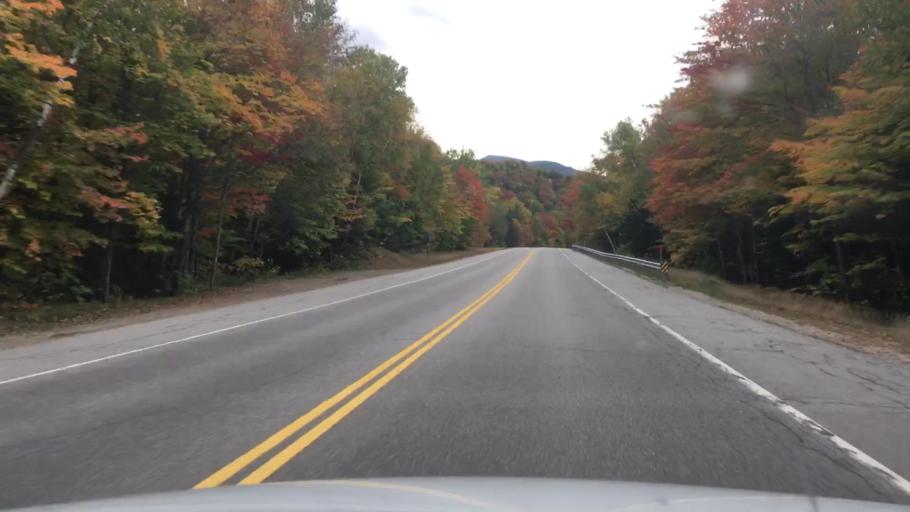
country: US
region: New Hampshire
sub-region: Coos County
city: Gorham
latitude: 44.3201
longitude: -71.2173
